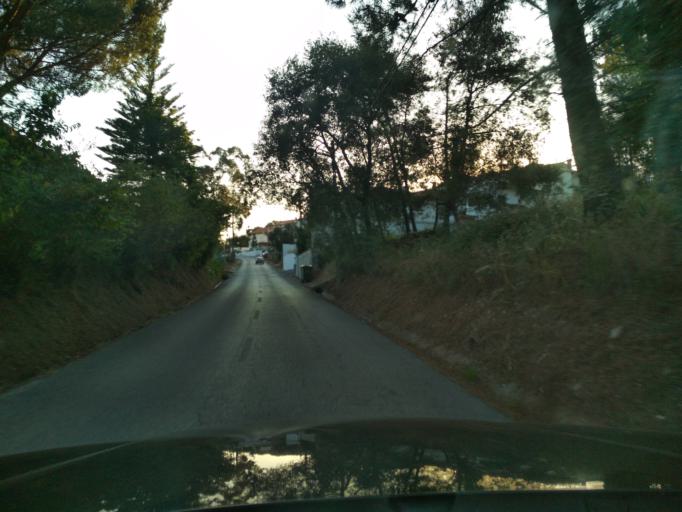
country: PT
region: Coimbra
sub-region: Coimbra
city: Coimbra
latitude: 40.2422
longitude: -8.4015
